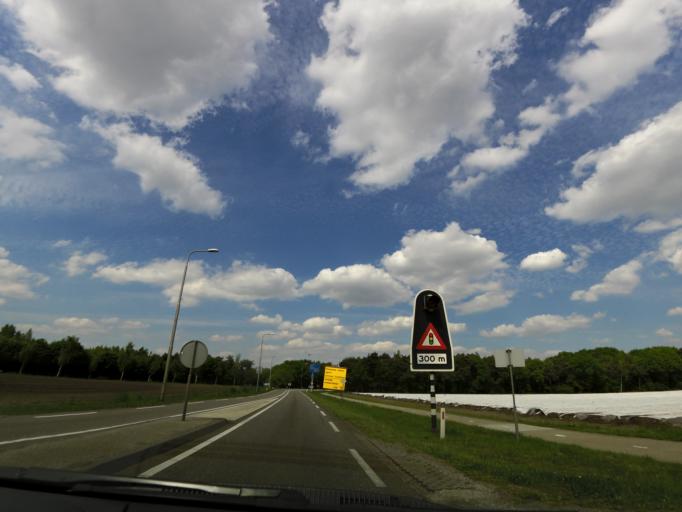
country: NL
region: Limburg
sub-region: Gemeente Peel en Maas
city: Maasbree
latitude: 51.3733
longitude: 5.9818
